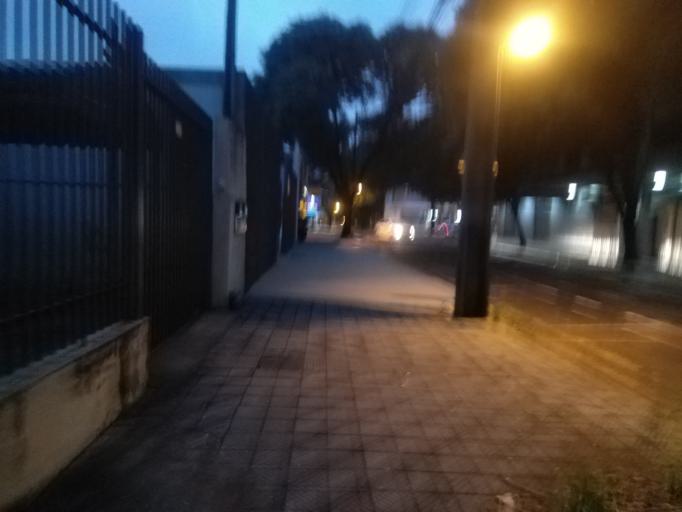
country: BR
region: Parana
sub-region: Maringa
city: Maringa
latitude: -23.4136
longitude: -51.9311
